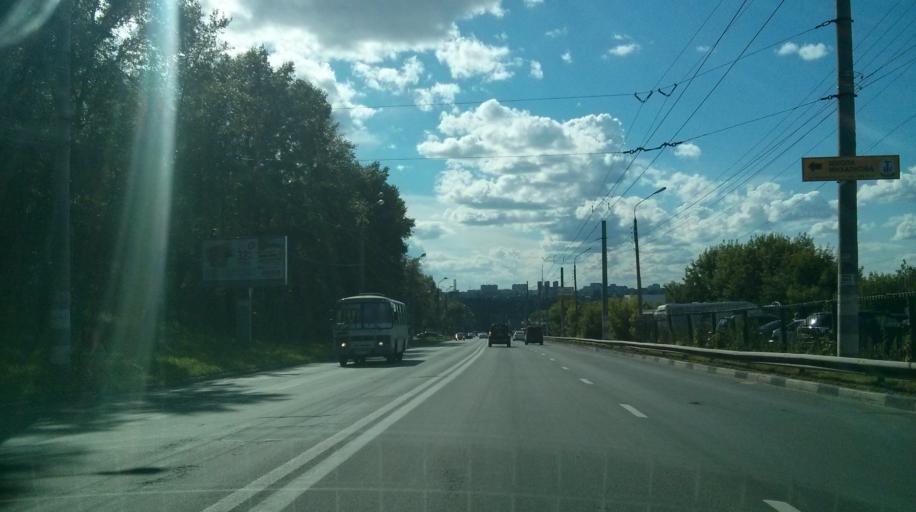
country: RU
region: Nizjnij Novgorod
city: Afonino
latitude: 56.2995
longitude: 44.0728
